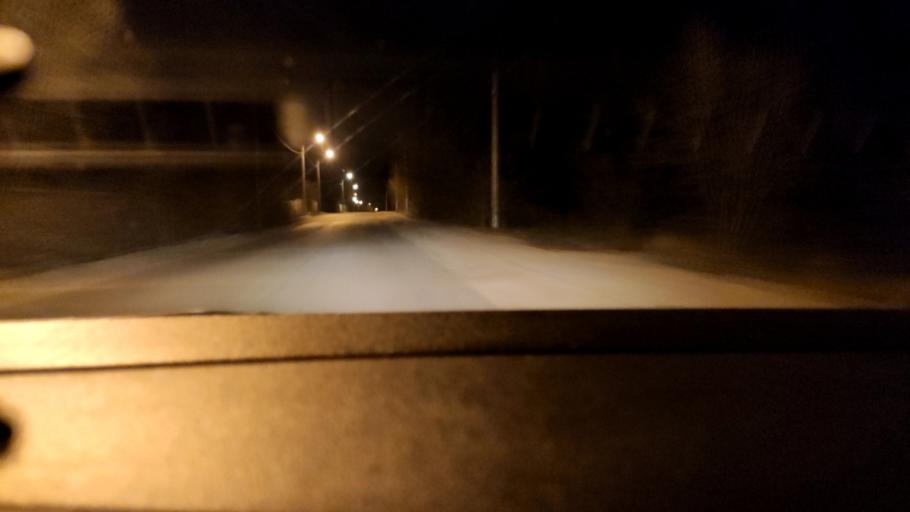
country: RU
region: Voronezj
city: Pridonskoy
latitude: 51.6907
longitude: 39.1037
